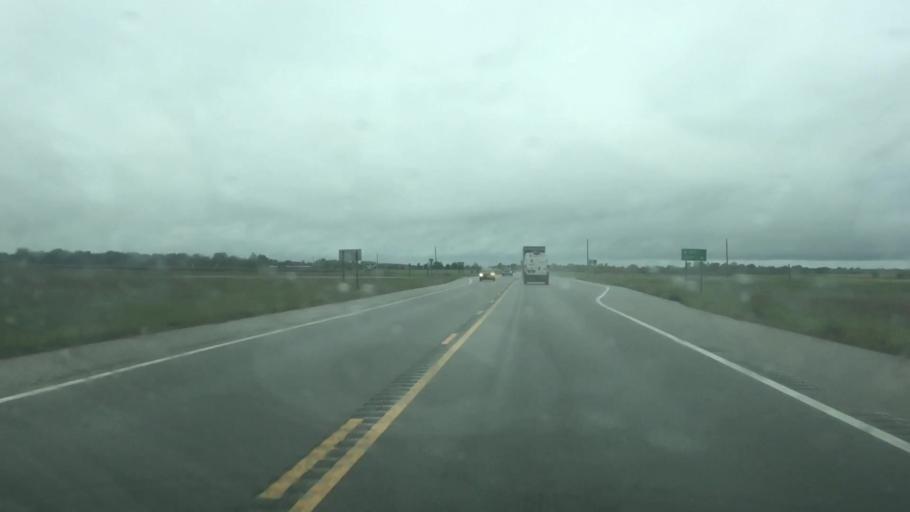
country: US
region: Kansas
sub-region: Allen County
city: Iola
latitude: 38.0829
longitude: -95.3692
